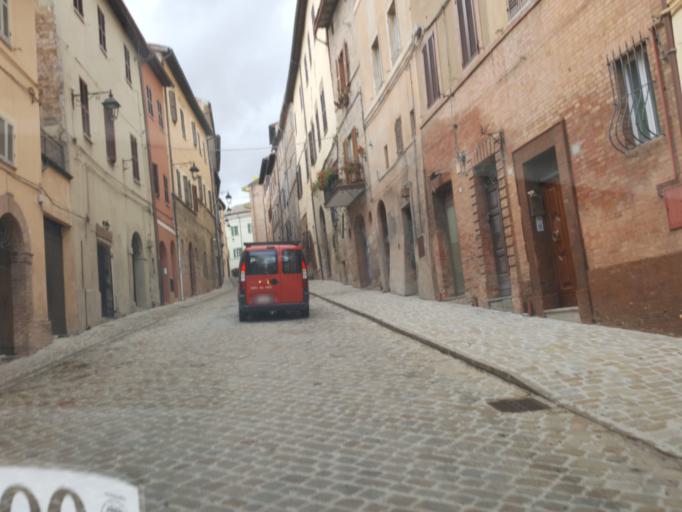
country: IT
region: The Marches
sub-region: Provincia di Macerata
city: Camerino
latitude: 43.1379
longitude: 13.0727
